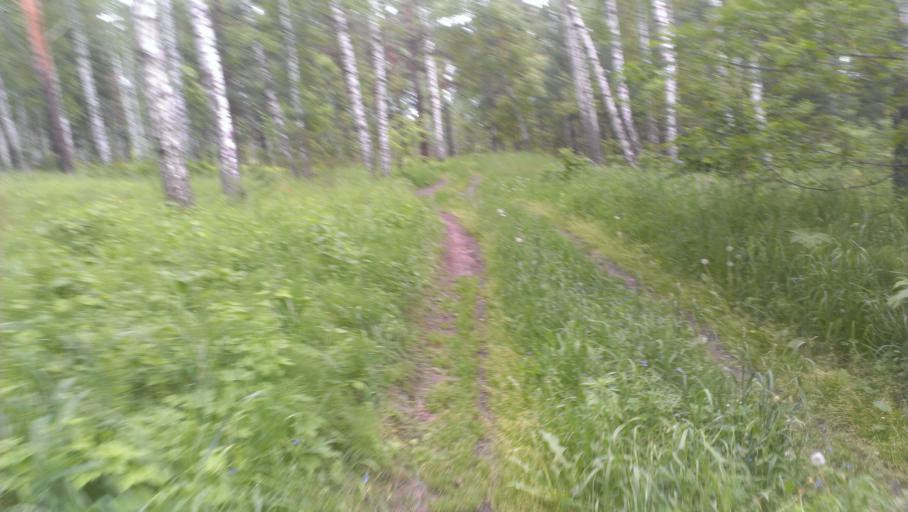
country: RU
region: Altai Krai
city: Sannikovo
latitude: 53.3387
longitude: 84.0500
